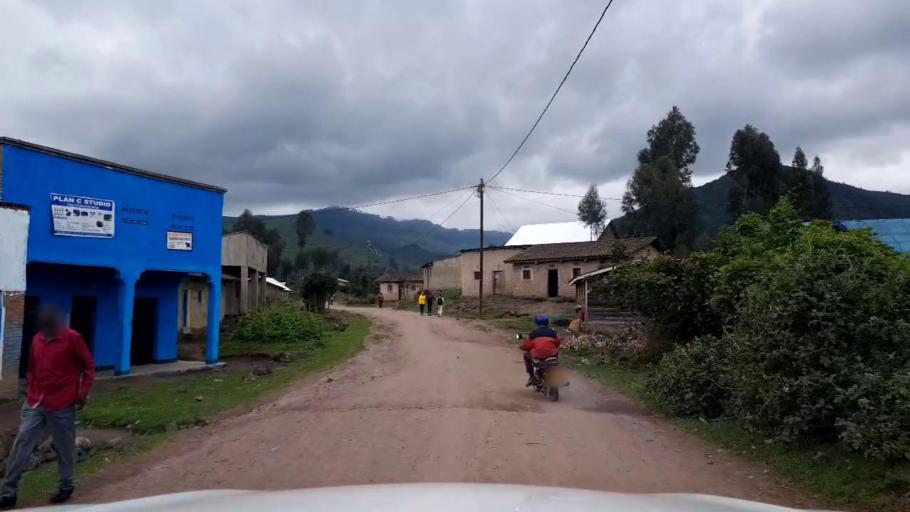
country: RW
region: Western Province
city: Gisenyi
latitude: -1.6371
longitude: 29.4056
